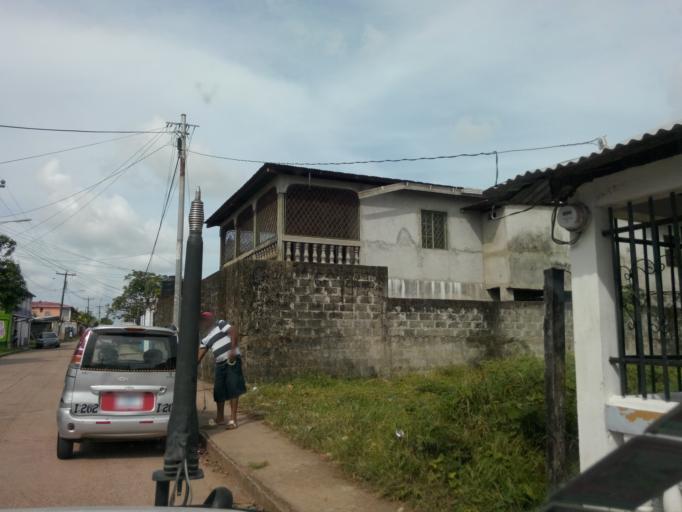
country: NI
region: Atlantico Sur
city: Bluefields
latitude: 11.9955
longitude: -83.7705
